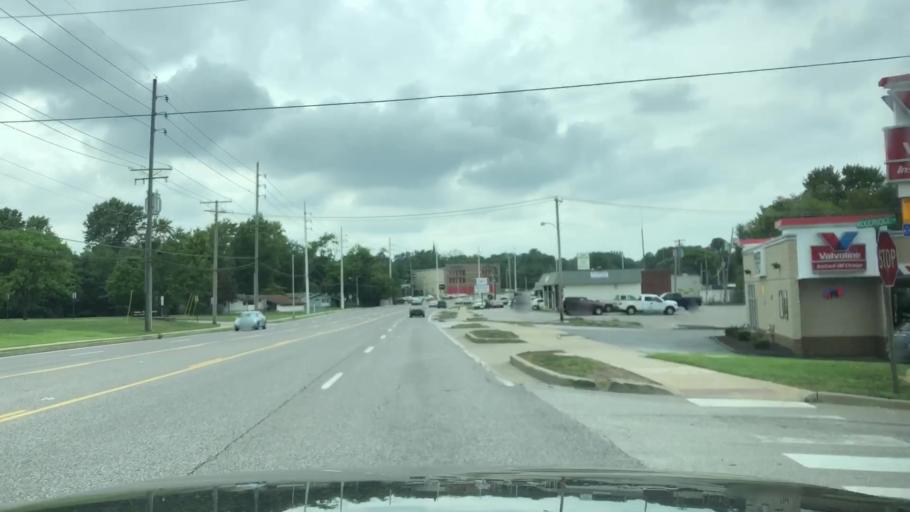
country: US
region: Missouri
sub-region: Saint Louis County
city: Florissant
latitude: 38.7994
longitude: -90.3174
